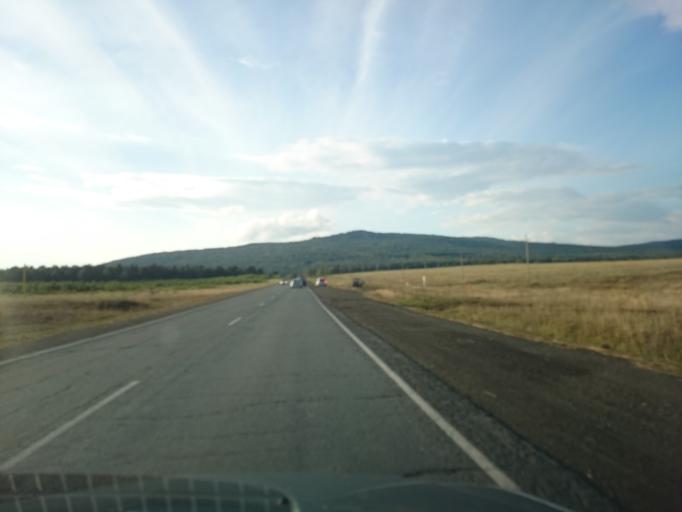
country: RU
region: Bashkortostan
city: Lomovka
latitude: 53.8884
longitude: 58.0969
